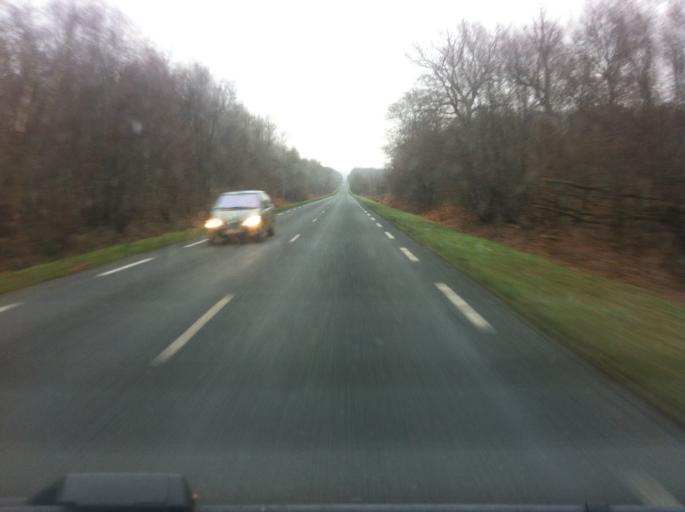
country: FR
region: Haute-Normandie
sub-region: Departement de la Seine-Maritime
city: La Mailleraye-sur-Seine
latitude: 49.4568
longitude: 0.7839
